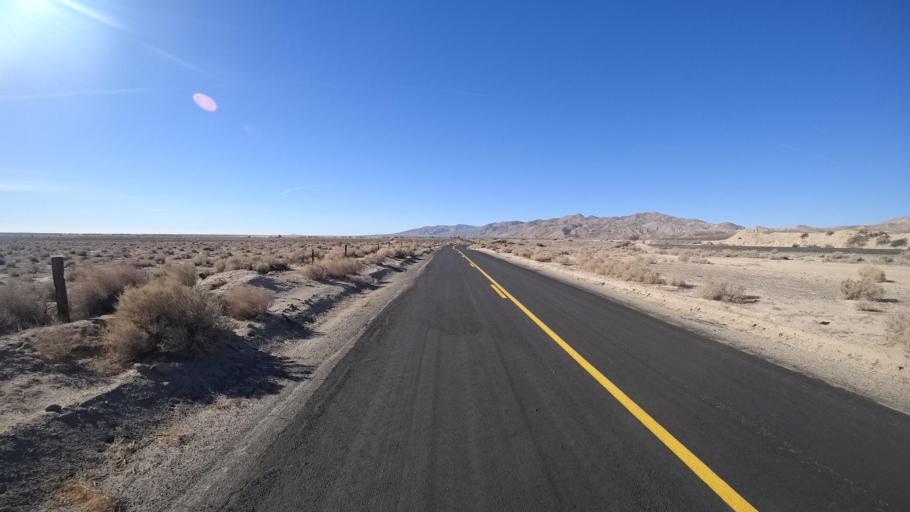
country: US
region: California
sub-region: Kern County
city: California City
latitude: 35.3041
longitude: -117.9758
